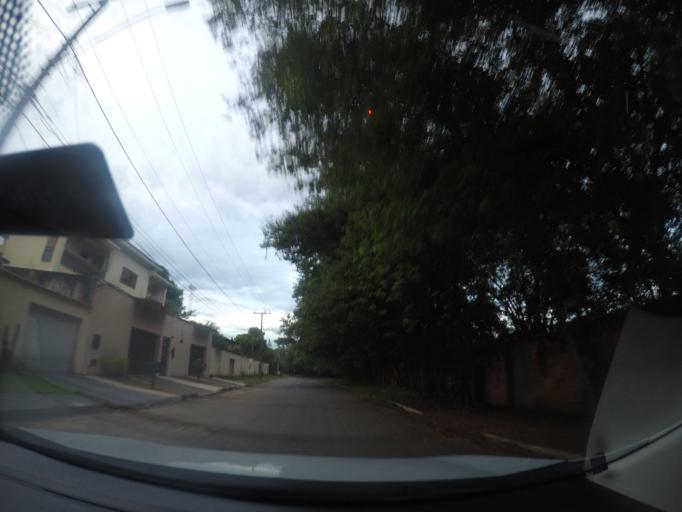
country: BR
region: Goias
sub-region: Goiania
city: Goiania
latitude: -16.6471
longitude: -49.2231
